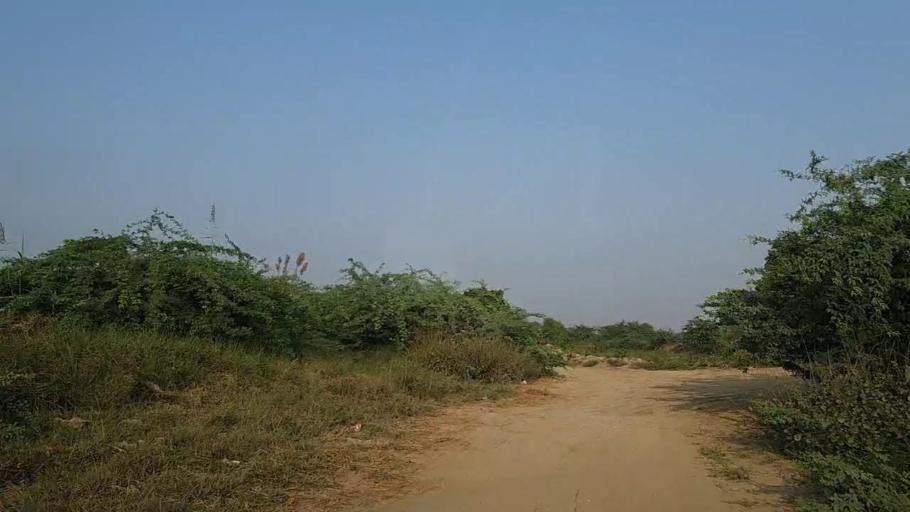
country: PK
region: Sindh
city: Thatta
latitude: 24.6634
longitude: 67.7761
